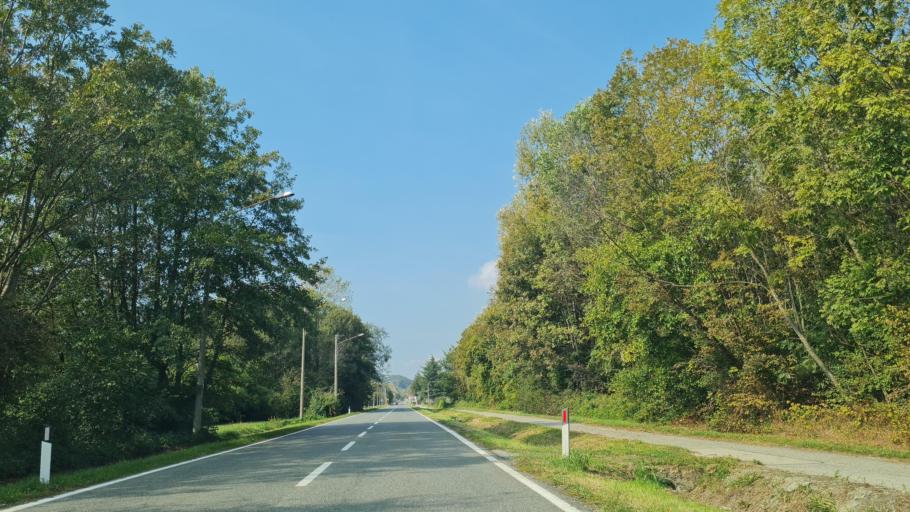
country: IT
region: Piedmont
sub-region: Provincia di Torino
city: Caprie
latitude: 45.1183
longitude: 7.3444
